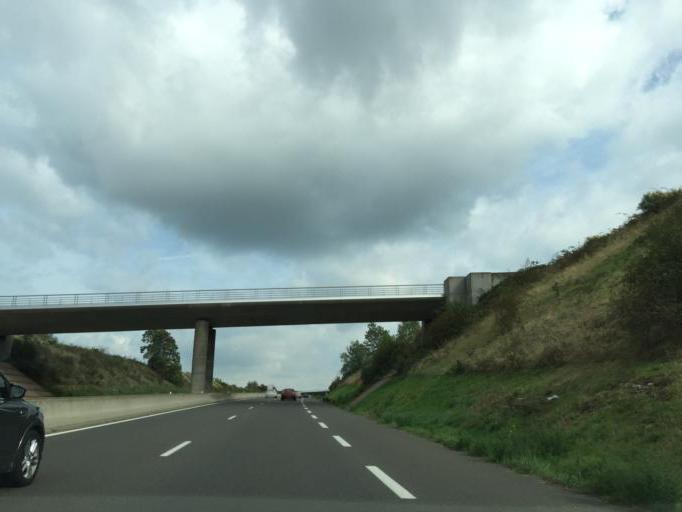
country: FR
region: Rhone-Alpes
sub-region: Departement de la Loire
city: Andrezieux-Boutheon
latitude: 45.5187
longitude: 4.2741
